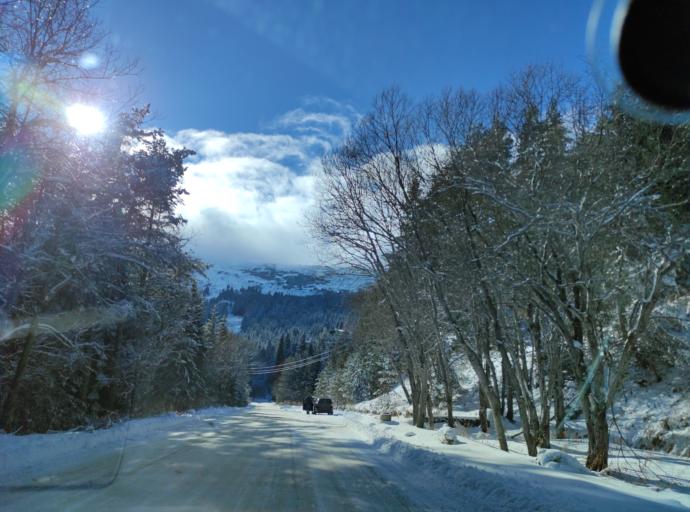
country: BG
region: Sofia-Capital
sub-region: Stolichna Obshtina
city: Sofia
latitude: 42.5900
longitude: 23.2984
